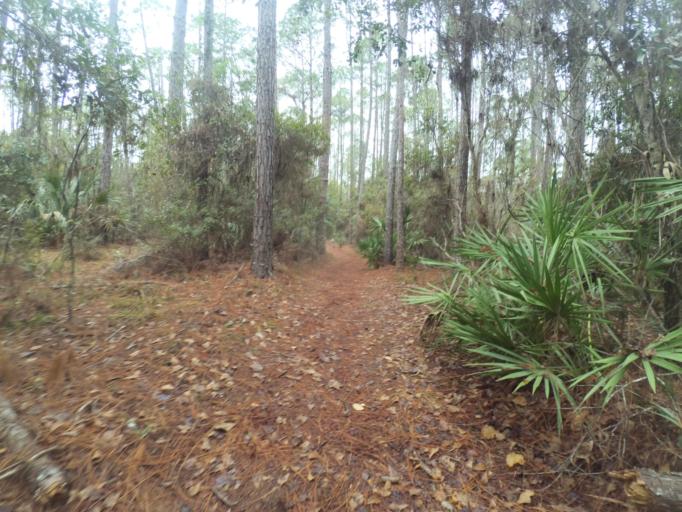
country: US
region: Florida
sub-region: Alachua County
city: Gainesville
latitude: 29.5381
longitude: -82.2852
